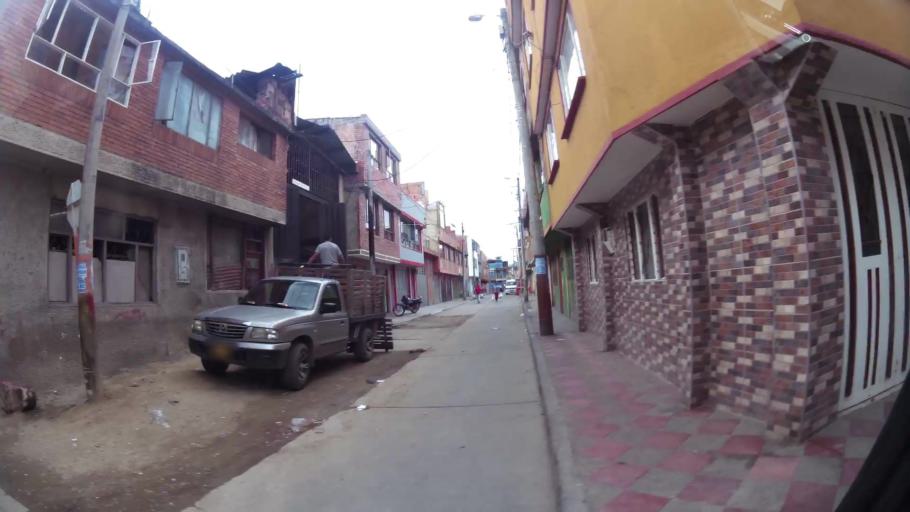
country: CO
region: Cundinamarca
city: Cota
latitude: 4.7246
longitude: -74.0941
